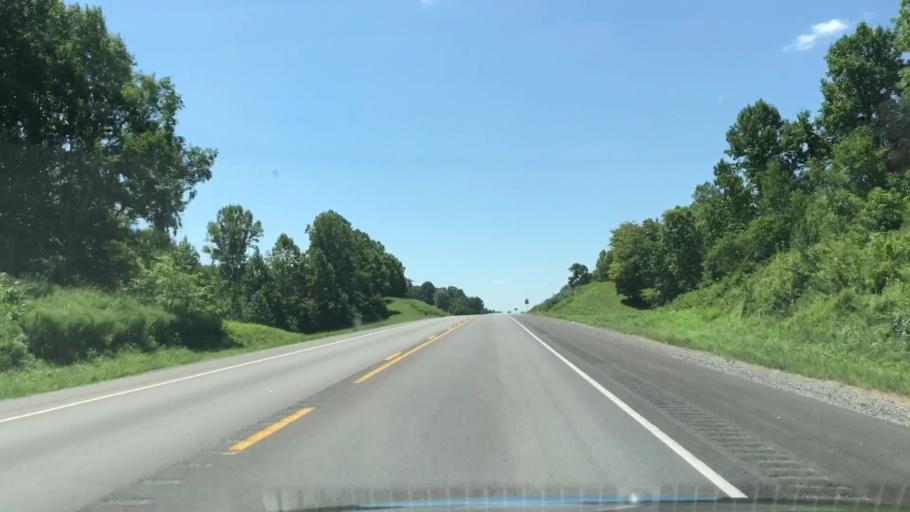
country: US
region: Kentucky
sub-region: Cumberland County
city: Burkesville
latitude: 36.6598
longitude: -85.3714
